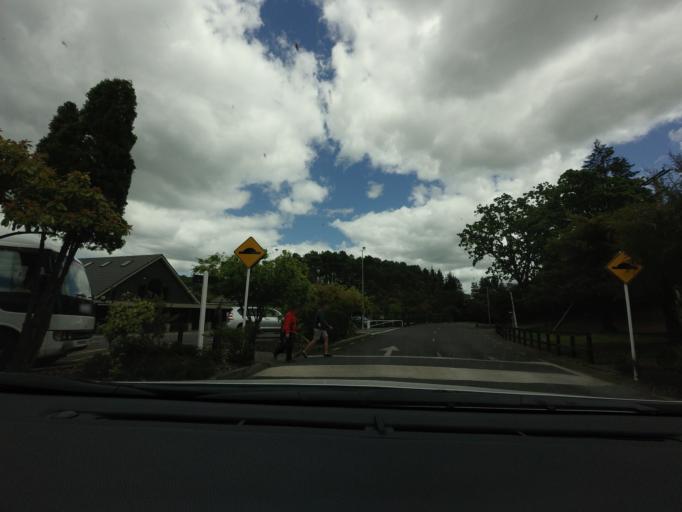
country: NZ
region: Bay of Plenty
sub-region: Rotorua District
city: Rotorua
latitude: -38.3555
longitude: 176.3674
